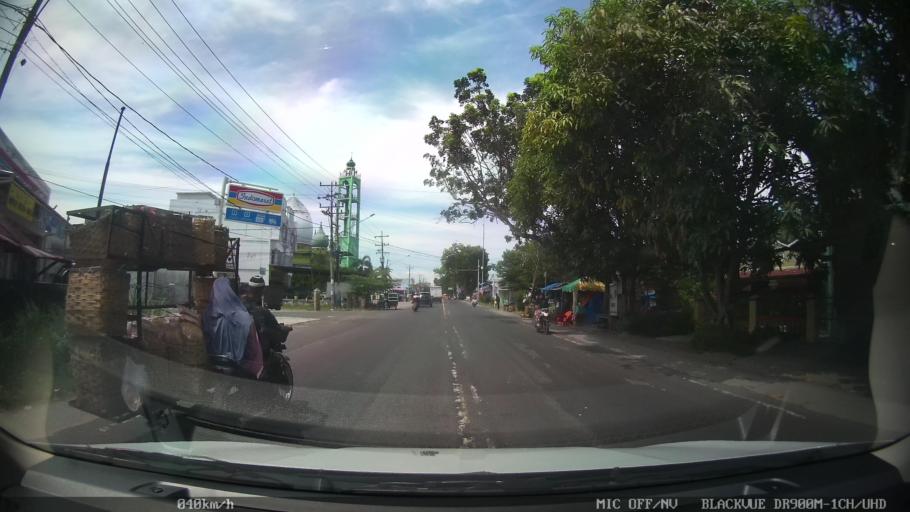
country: ID
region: North Sumatra
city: Binjai
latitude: 3.6297
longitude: 98.5102
